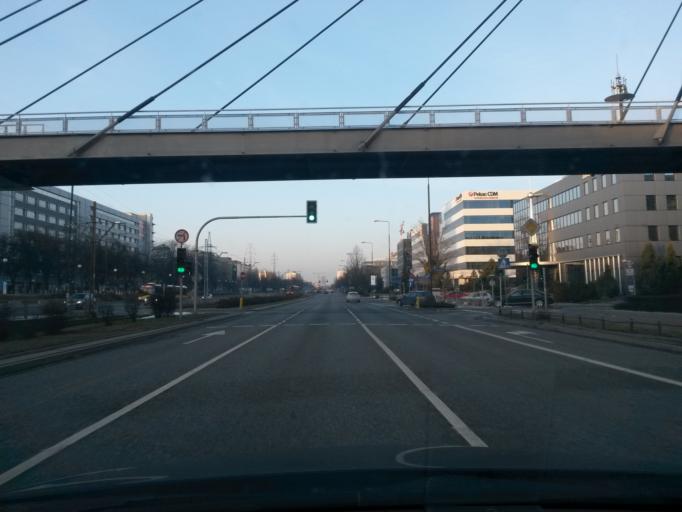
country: PL
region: Masovian Voivodeship
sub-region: Warszawa
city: Mokotow
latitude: 52.1806
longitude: 21.0025
